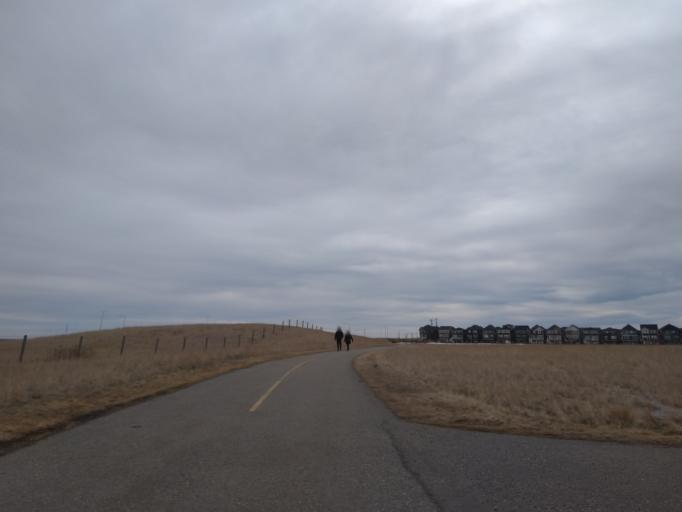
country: CA
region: Alberta
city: Chestermere
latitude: 51.1355
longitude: -113.9257
